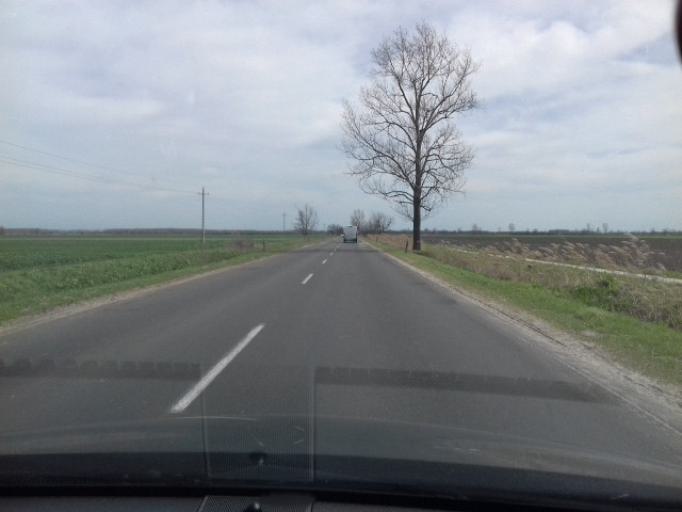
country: HU
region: Jasz-Nagykun-Szolnok
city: Cserkeszolo
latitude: 46.8569
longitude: 20.2288
